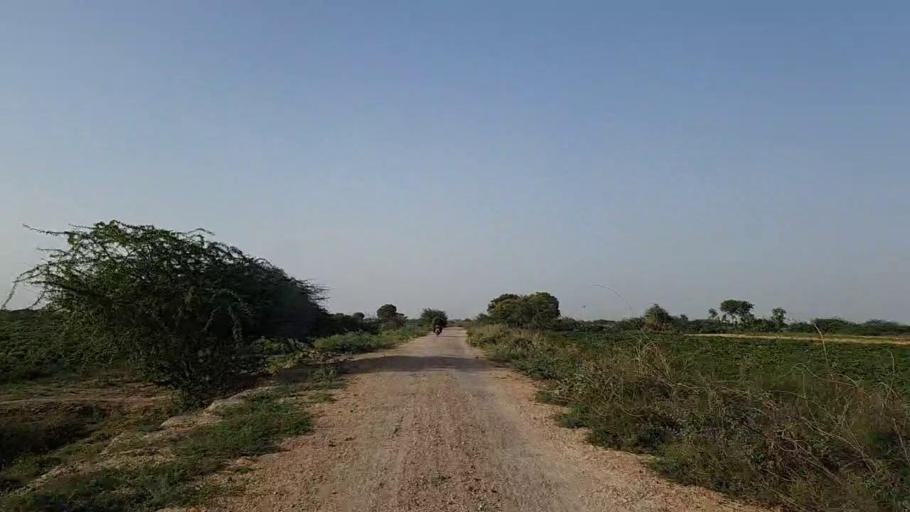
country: PK
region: Sindh
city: Jati
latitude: 24.3154
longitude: 68.1690
